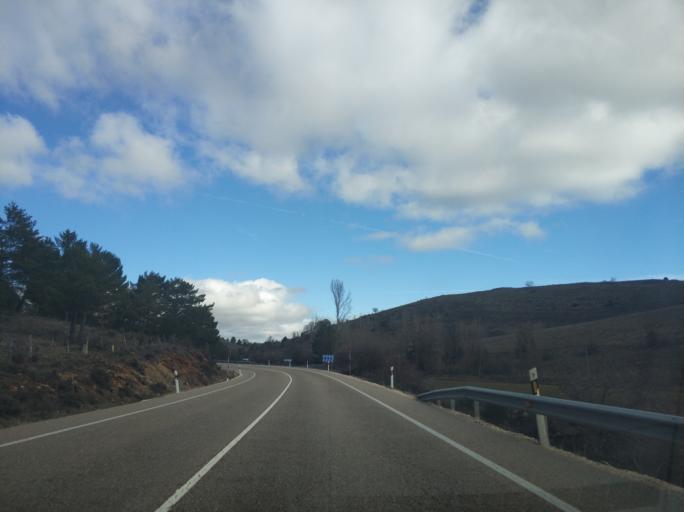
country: ES
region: Castille and Leon
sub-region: Provincia de Burgos
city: Rabanera del Pinar
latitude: 41.8759
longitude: -3.2213
